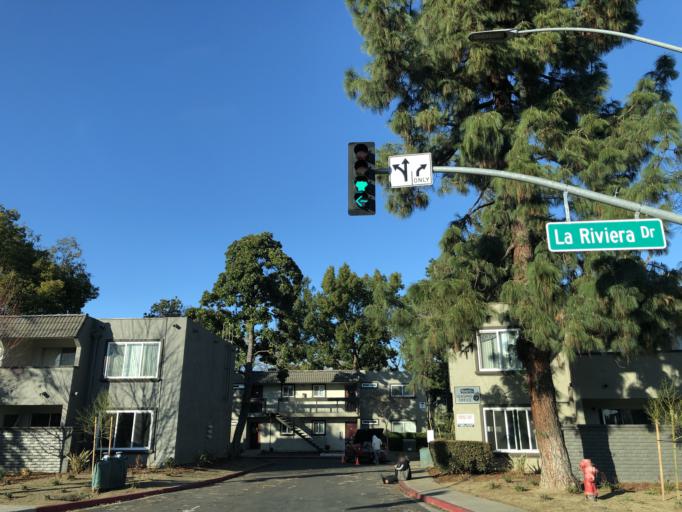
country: US
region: California
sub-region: Sacramento County
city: Rosemont
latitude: 38.5641
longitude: -121.3812
